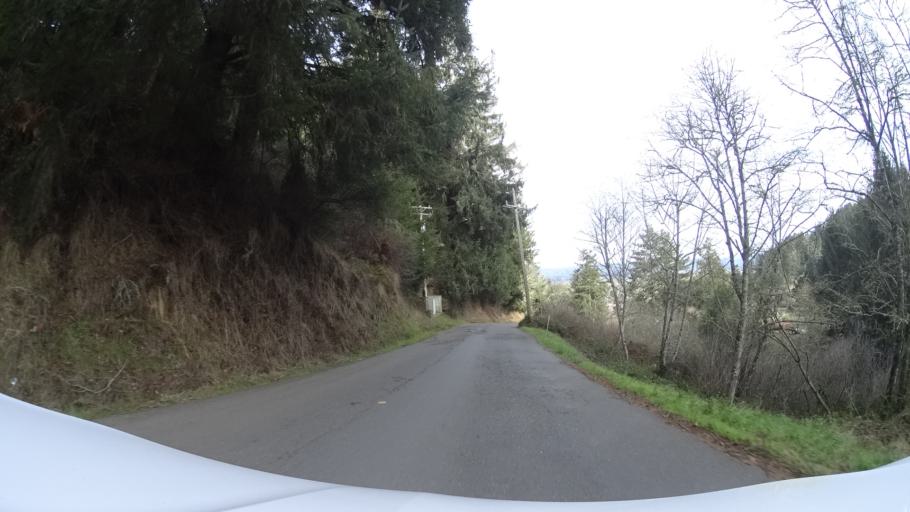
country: US
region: California
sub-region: Humboldt County
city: Ferndale
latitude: 40.5733
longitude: -124.2697
